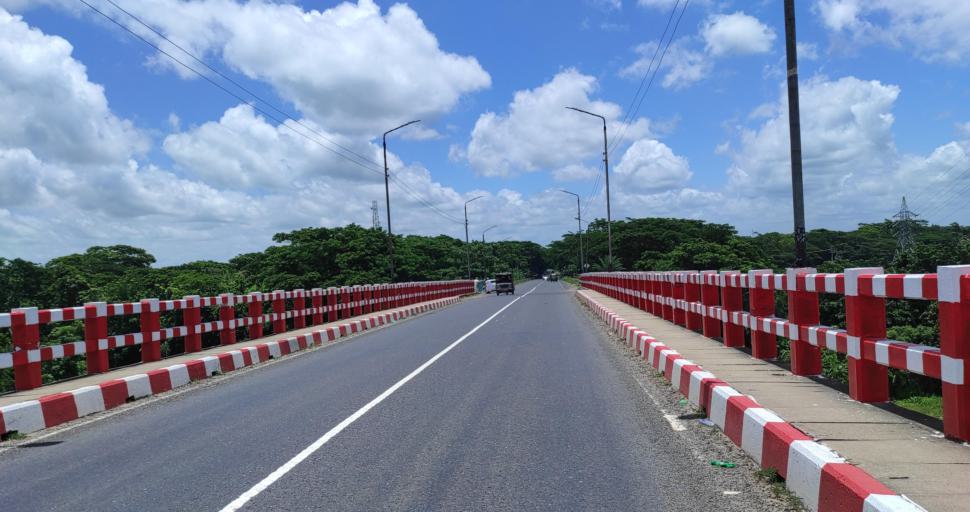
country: BD
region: Barisal
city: Gaurnadi
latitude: 22.8238
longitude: 90.2642
